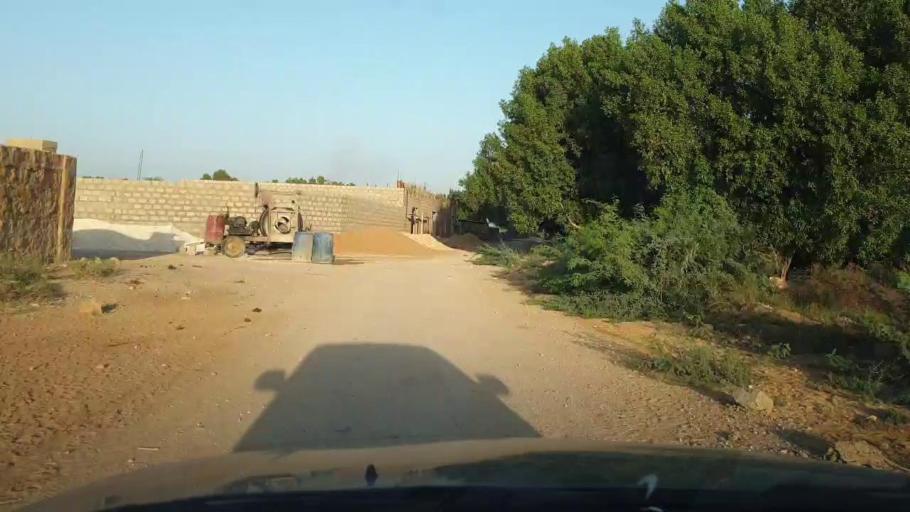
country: PK
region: Sindh
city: Kotri
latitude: 25.2222
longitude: 68.2312
